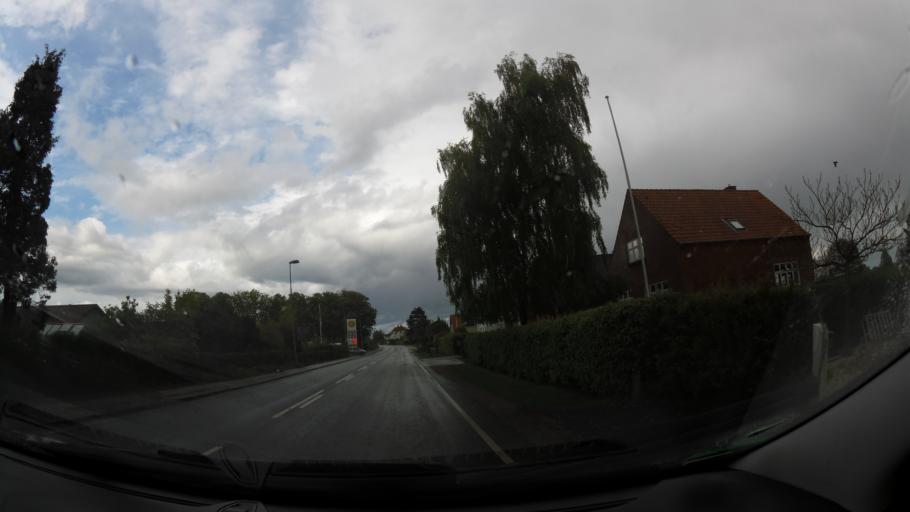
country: DK
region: South Denmark
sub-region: Nyborg Kommune
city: Nyborg
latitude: 55.3027
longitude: 10.7819
